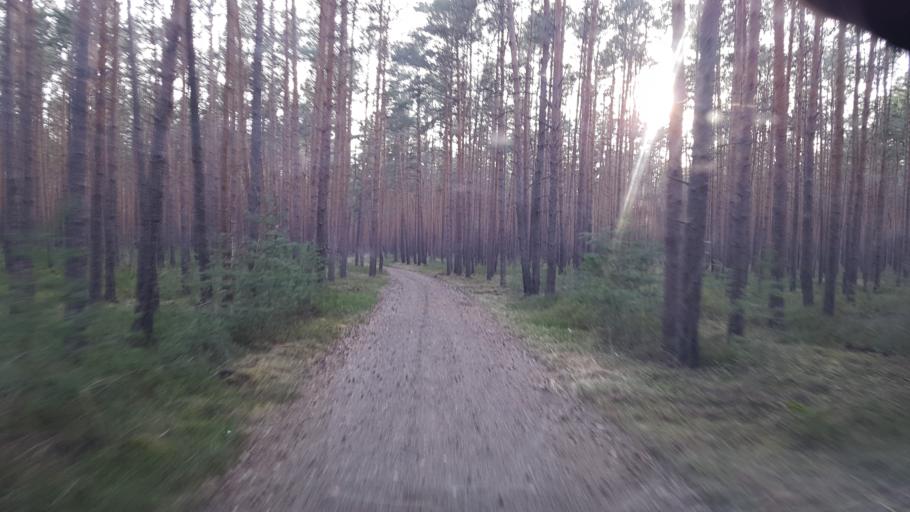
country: DE
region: Brandenburg
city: Trobitz
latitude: 51.5679
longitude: 13.4603
